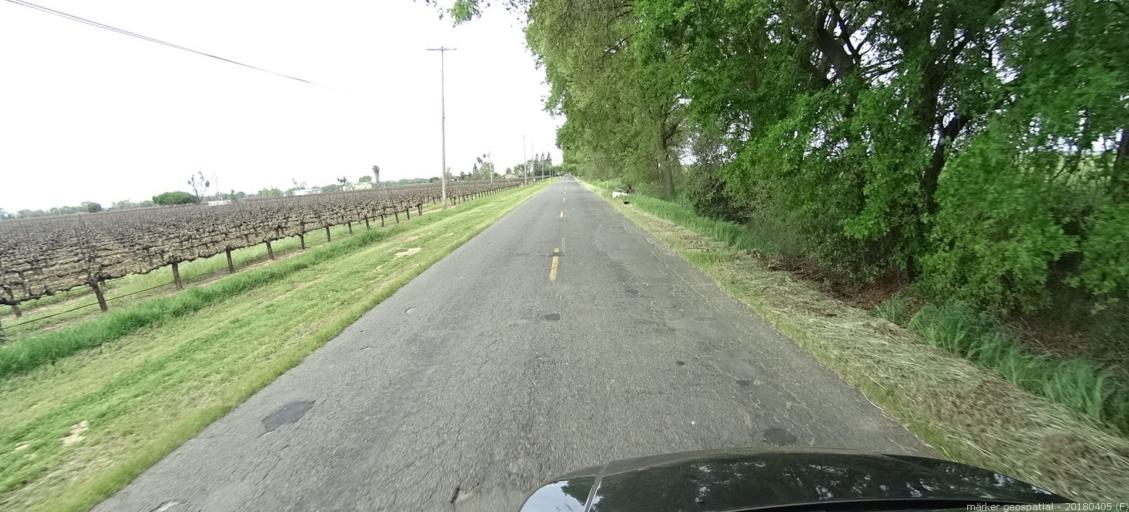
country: US
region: California
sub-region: Sacramento County
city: Galt
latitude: 38.2400
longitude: -121.3442
